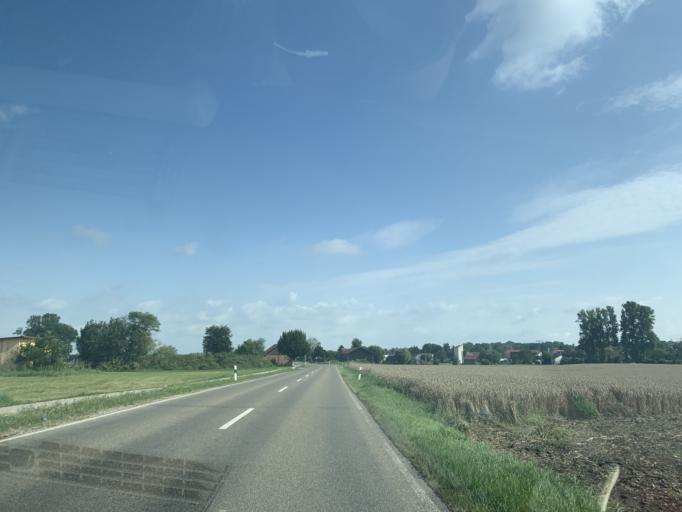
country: DE
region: Bavaria
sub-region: Swabia
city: Kissing
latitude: 48.2921
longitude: 10.9818
